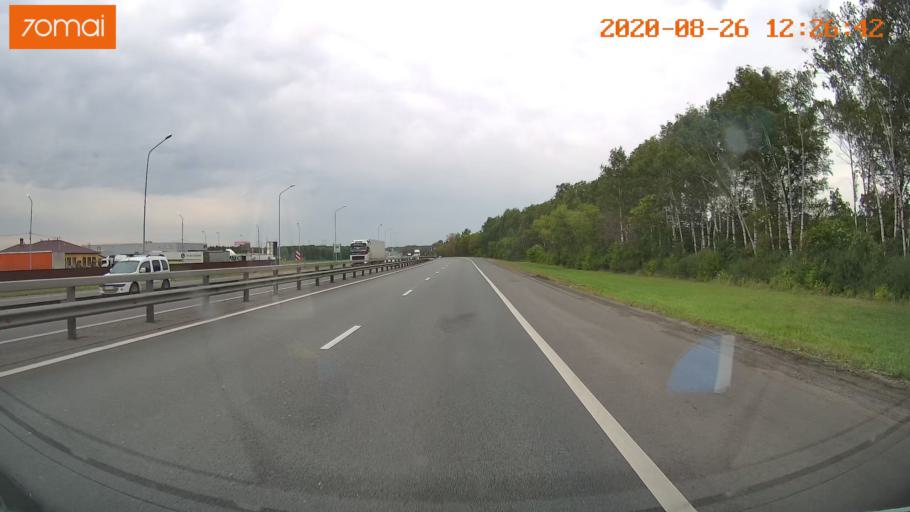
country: RU
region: Rjazan
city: Polyany
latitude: 54.5371
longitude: 39.8547
